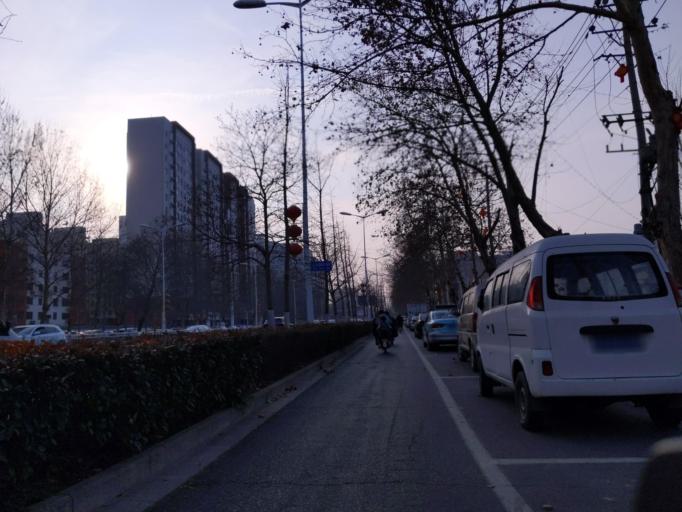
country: CN
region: Henan Sheng
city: Puyang
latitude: 35.7814
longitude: 115.0176
